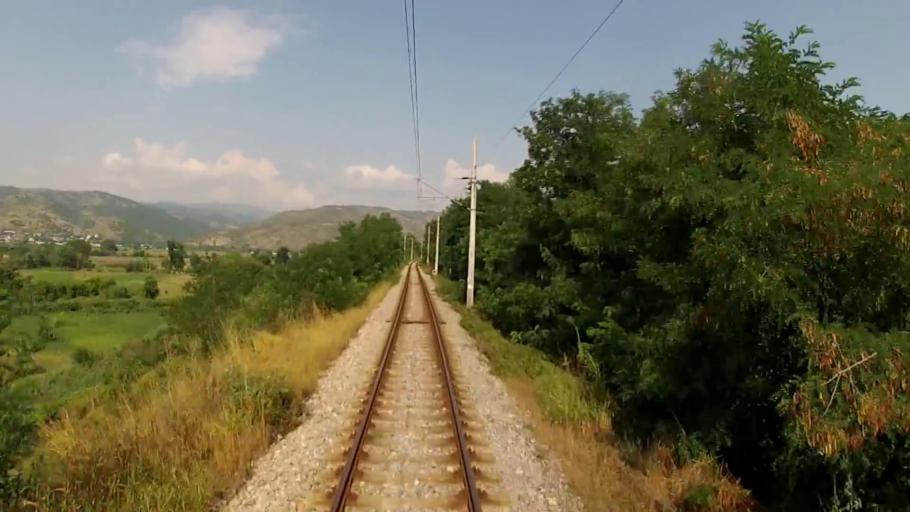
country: BG
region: Blagoevgrad
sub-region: Obshtina Sandanski
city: Sandanski
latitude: 41.5278
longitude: 23.2636
